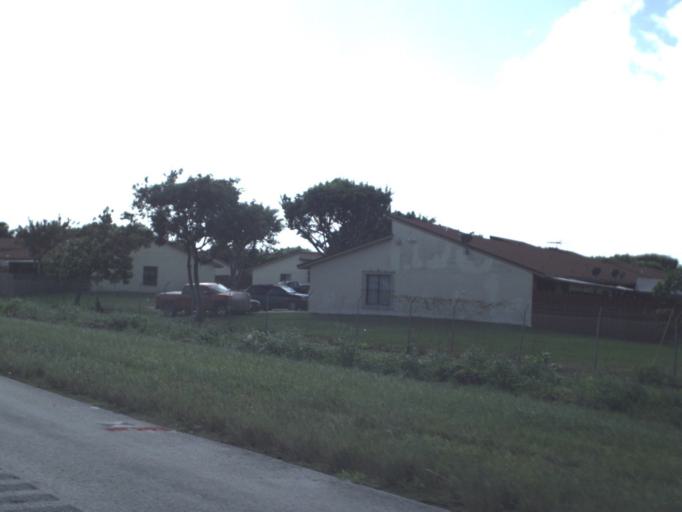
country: US
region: Florida
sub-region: Miami-Dade County
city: Naranja
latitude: 25.5069
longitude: -80.4163
